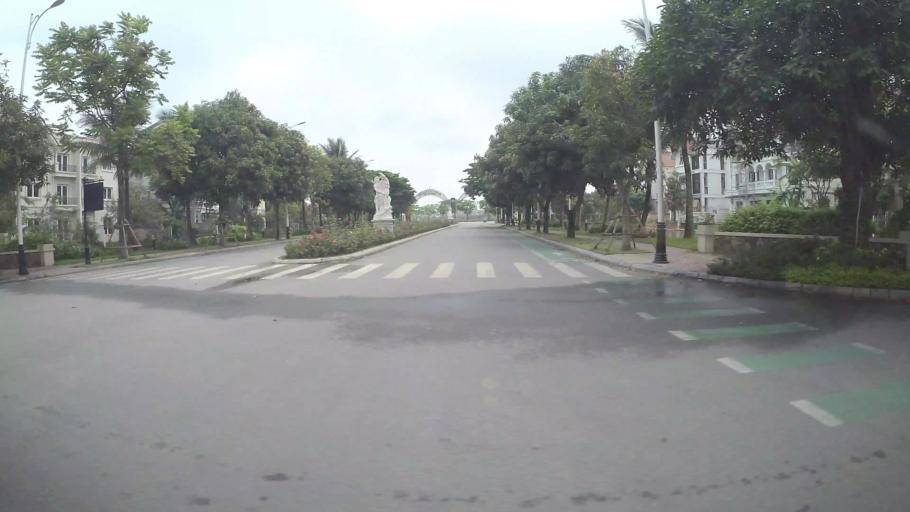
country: VN
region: Ha Noi
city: Trau Quy
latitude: 21.0457
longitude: 105.9188
